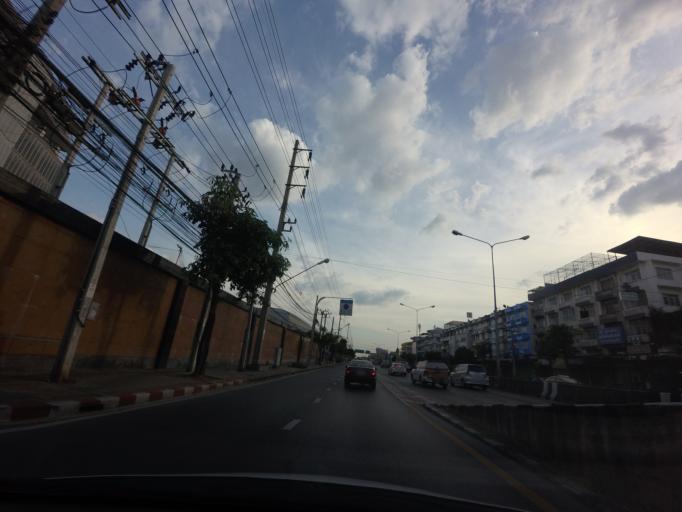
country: TH
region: Bangkok
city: Bang Khun Thian
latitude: 13.6538
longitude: 100.4306
